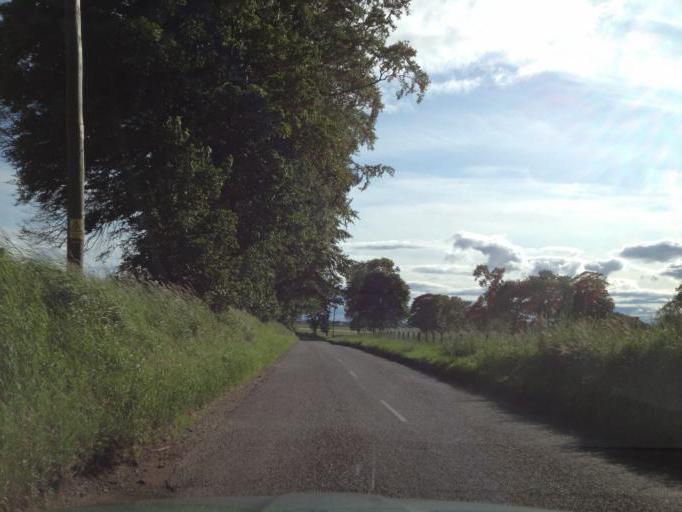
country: GB
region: Scotland
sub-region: Aberdeenshire
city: Laurencekirk
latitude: 56.8464
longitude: -2.5869
